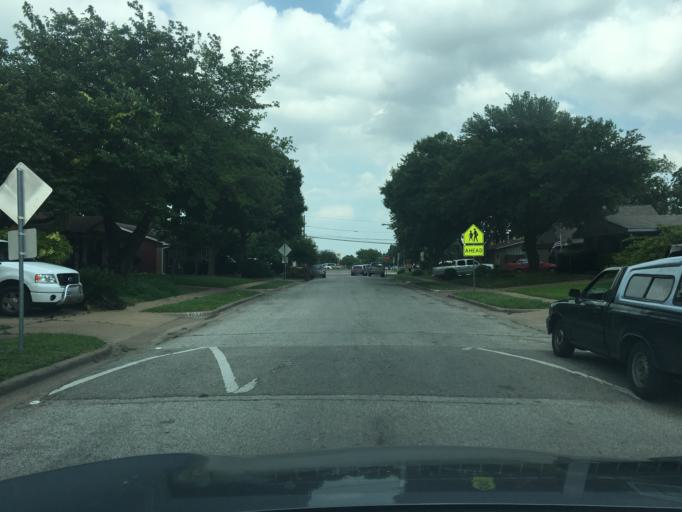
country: US
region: Texas
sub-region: Dallas County
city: Garland
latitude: 32.9141
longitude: -96.6841
